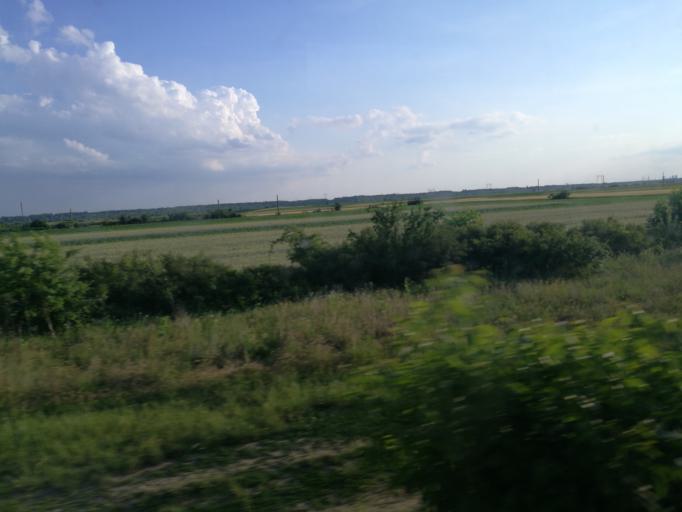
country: RO
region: Arges
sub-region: Comuna Calinesti
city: Calinesti
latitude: 44.8150
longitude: 25.0480
